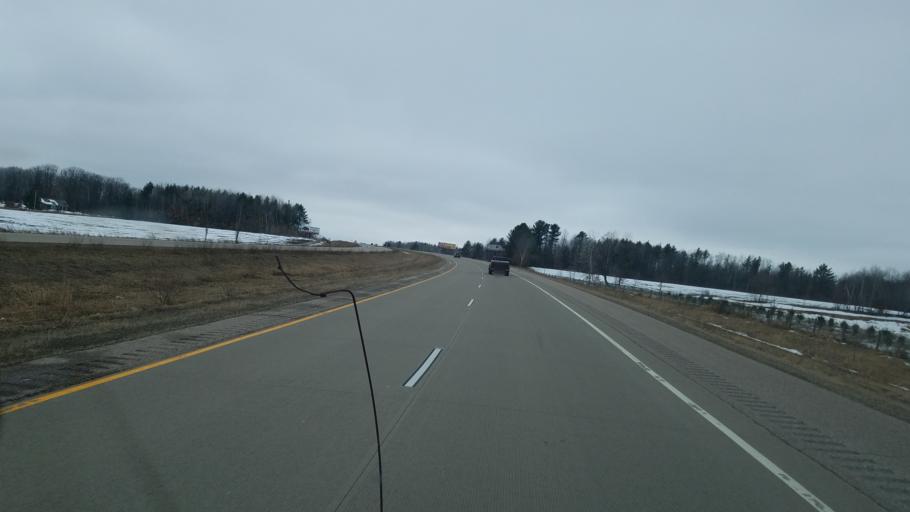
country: US
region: Wisconsin
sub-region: Portage County
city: Stevens Point
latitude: 44.6008
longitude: -89.6785
